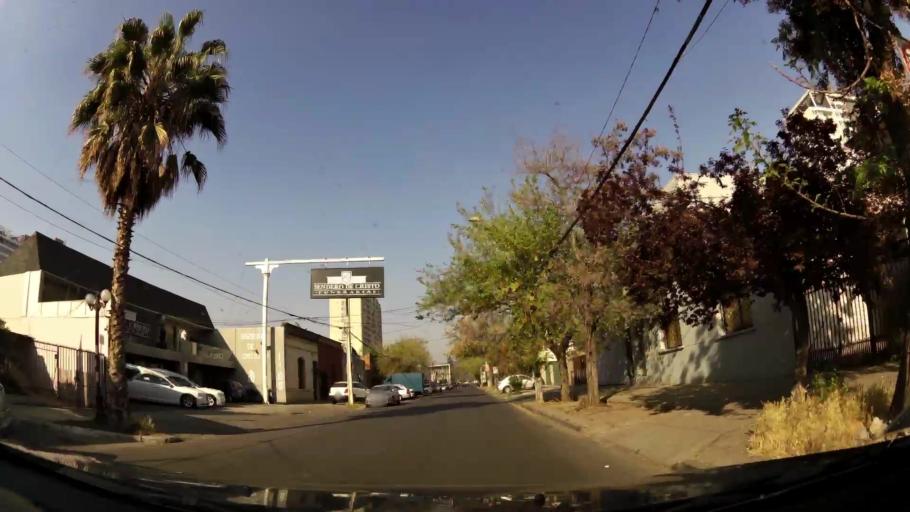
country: CL
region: Santiago Metropolitan
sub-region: Provincia de Santiago
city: Santiago
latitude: -33.4177
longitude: -70.6581
